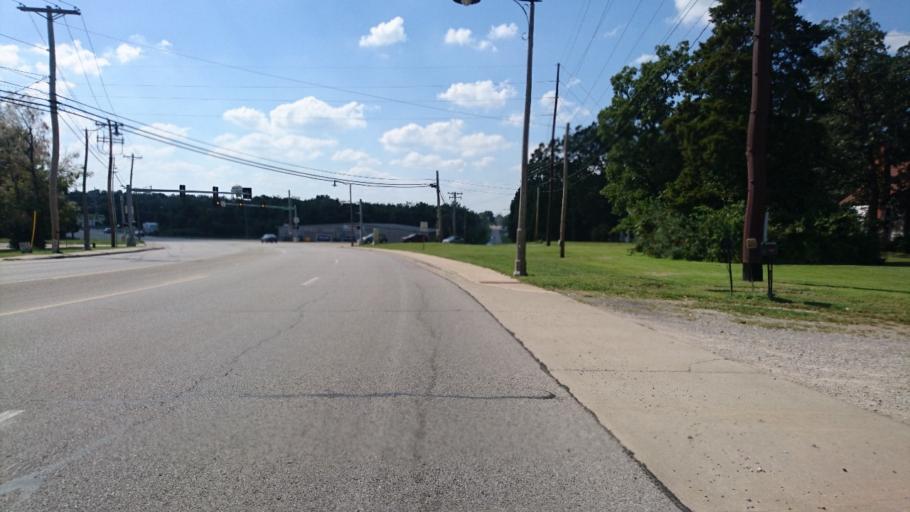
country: US
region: Missouri
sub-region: Laclede County
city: Lebanon
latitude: 37.6839
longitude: -92.6487
